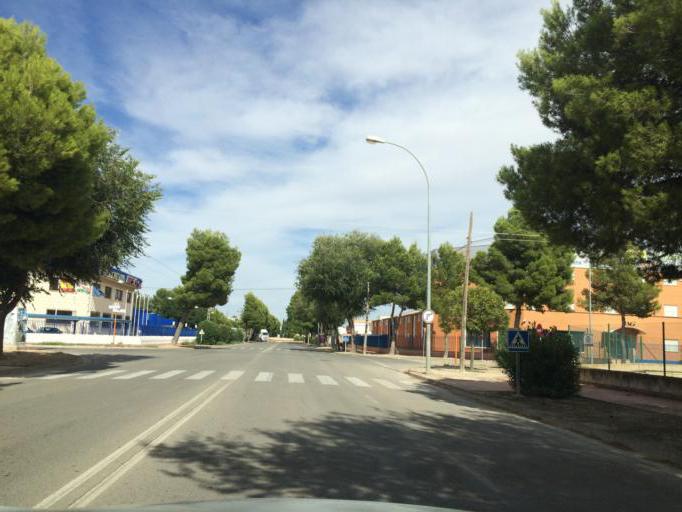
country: ES
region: Castille-La Mancha
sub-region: Provincia de Albacete
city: Albacete
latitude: 39.0164
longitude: -1.8848
